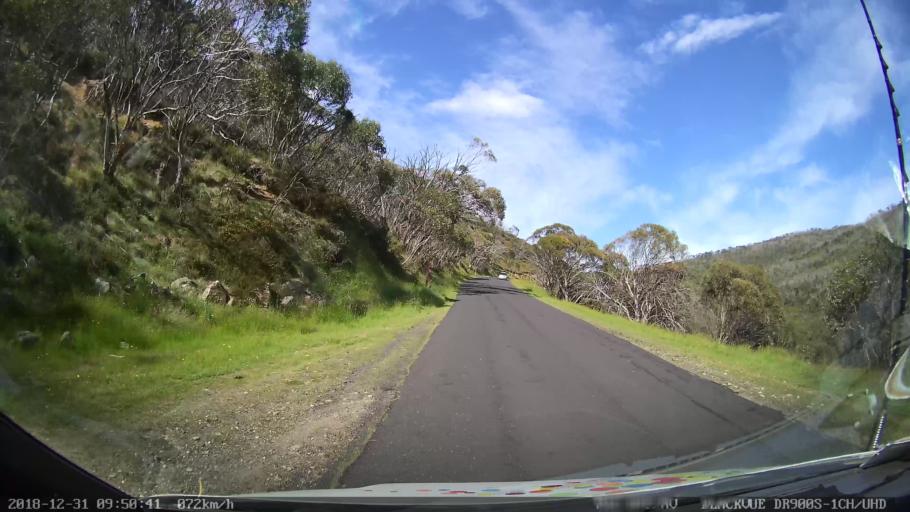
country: AU
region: New South Wales
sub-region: Snowy River
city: Jindabyne
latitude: -36.5214
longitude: 148.2702
